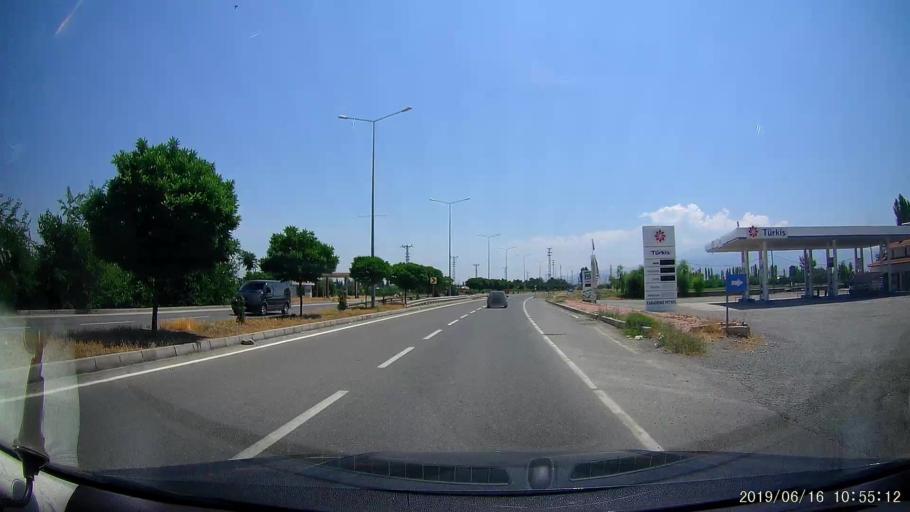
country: TR
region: Igdir
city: Igdir
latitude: 39.9373
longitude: 44.0077
